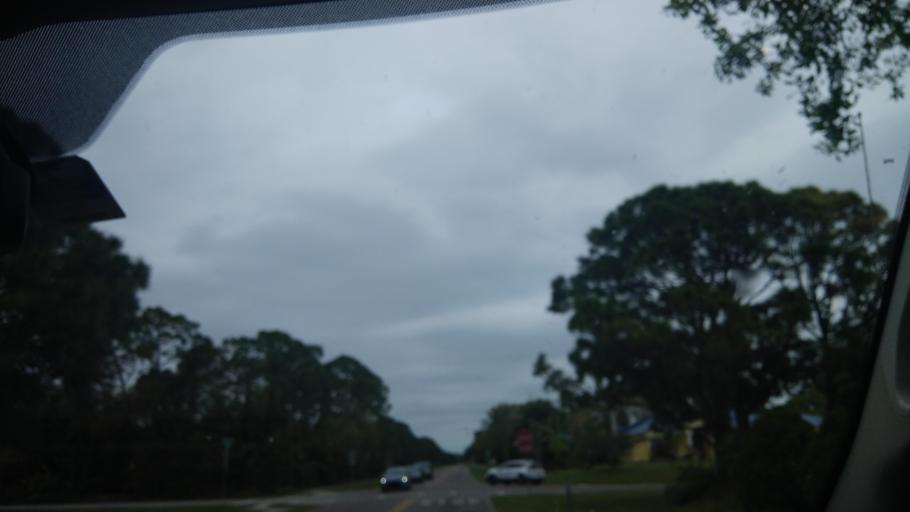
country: US
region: Florida
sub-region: Indian River County
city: Sebastian
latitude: 27.7723
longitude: -80.4953
